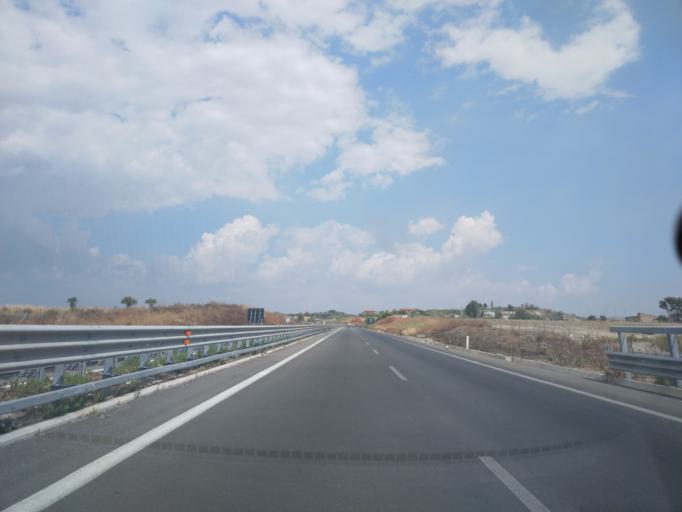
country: IT
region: Sicily
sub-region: Agrigento
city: Grotte
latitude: 37.3600
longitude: 13.6916
